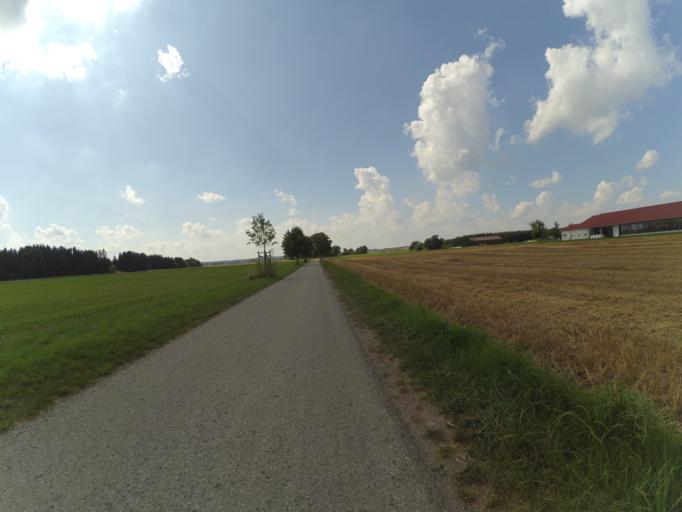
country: DE
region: Bavaria
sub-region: Swabia
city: Bad Worishofen
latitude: 48.0011
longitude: 10.6276
